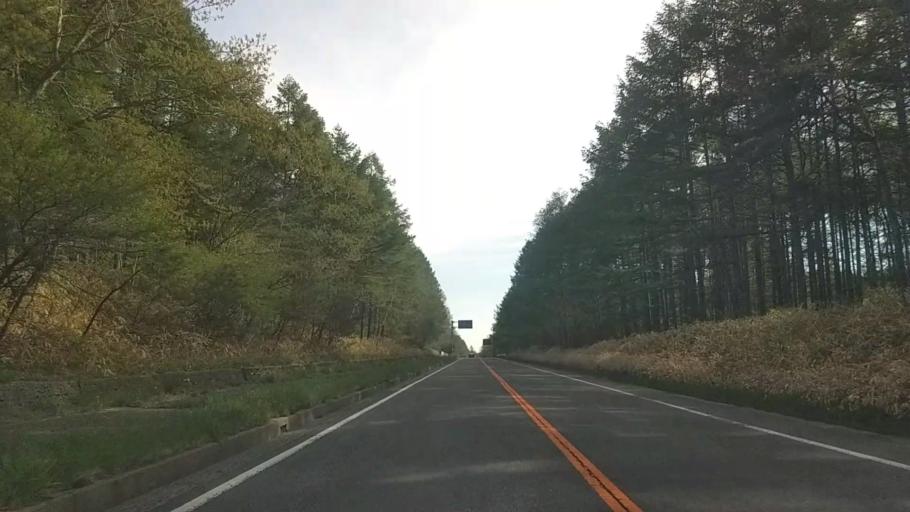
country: JP
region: Yamanashi
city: Nirasaki
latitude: 35.9366
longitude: 138.4480
